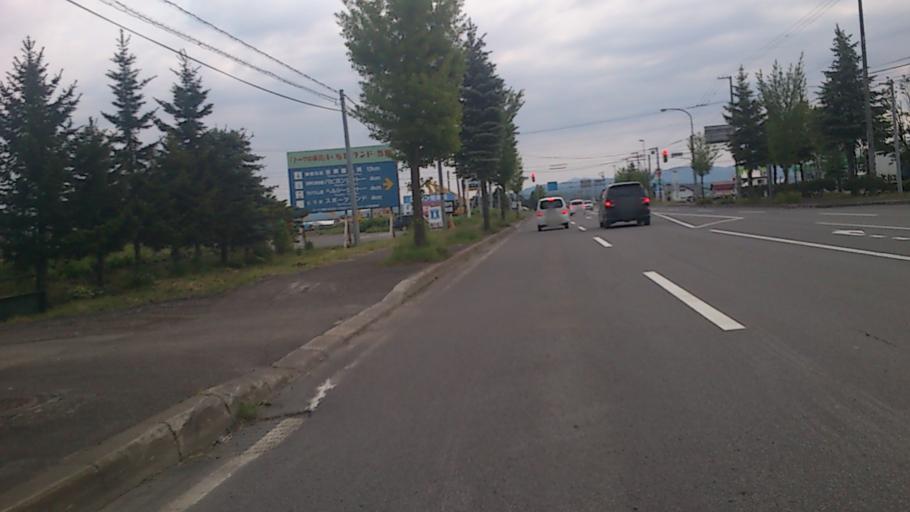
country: JP
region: Hokkaido
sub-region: Asahikawa-shi
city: Asahikawa
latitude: 43.8444
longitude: 142.4881
